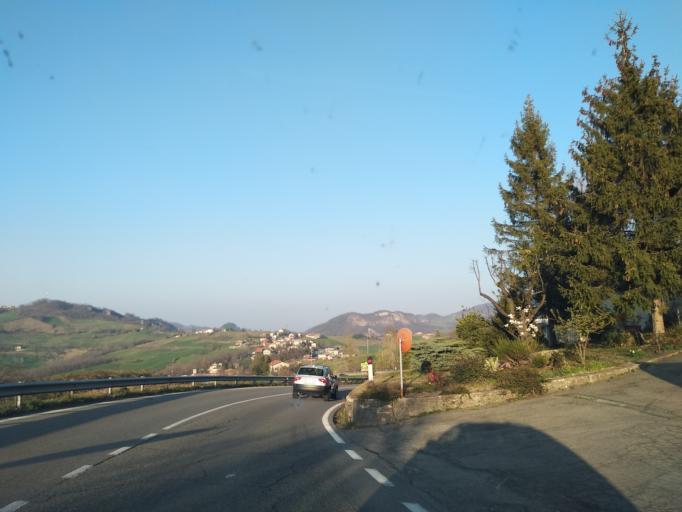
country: IT
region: Emilia-Romagna
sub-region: Provincia di Reggio Emilia
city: Castelnovo ne'Monti
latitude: 44.4330
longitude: 10.4188
